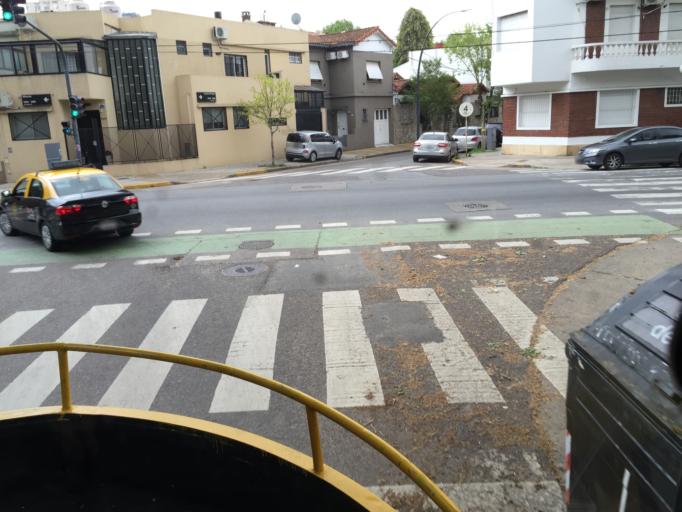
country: AR
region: Buenos Aires F.D.
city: Colegiales
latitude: -34.5525
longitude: -58.4497
